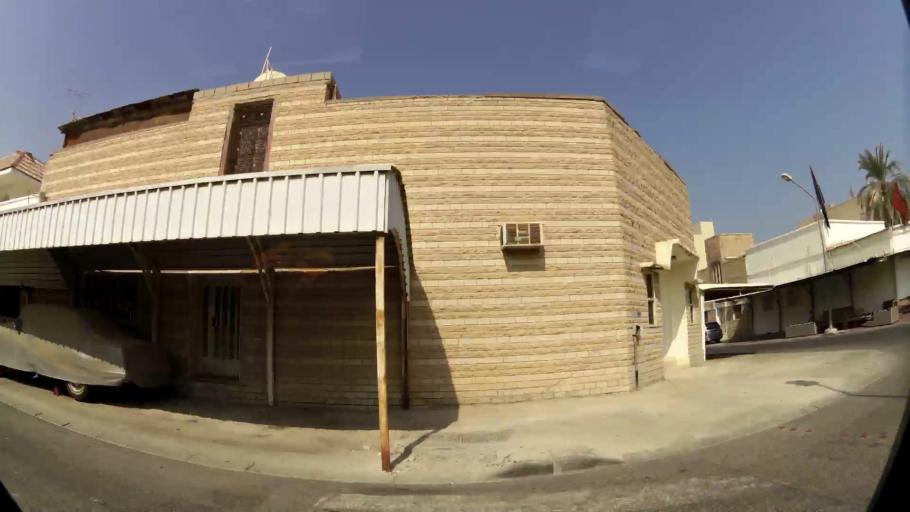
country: KW
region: Al Asimah
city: Ad Dasmah
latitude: 29.3601
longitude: 48.0145
